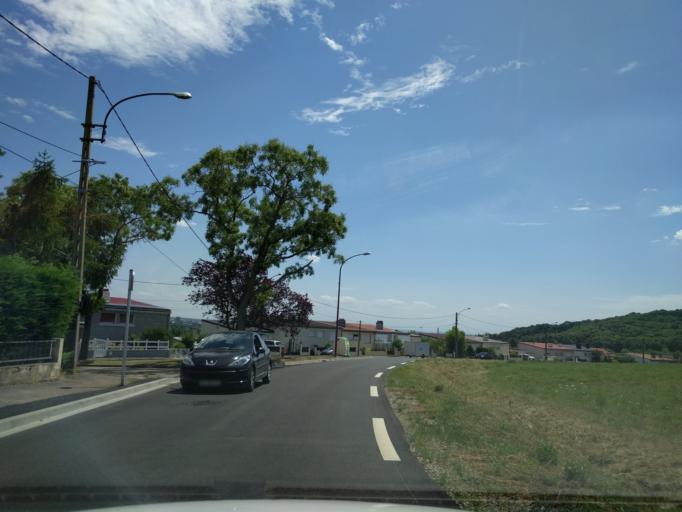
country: FR
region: Lorraine
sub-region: Departement de la Moselle
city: Le Ban Saint-Martin
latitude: 49.1331
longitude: 6.1426
